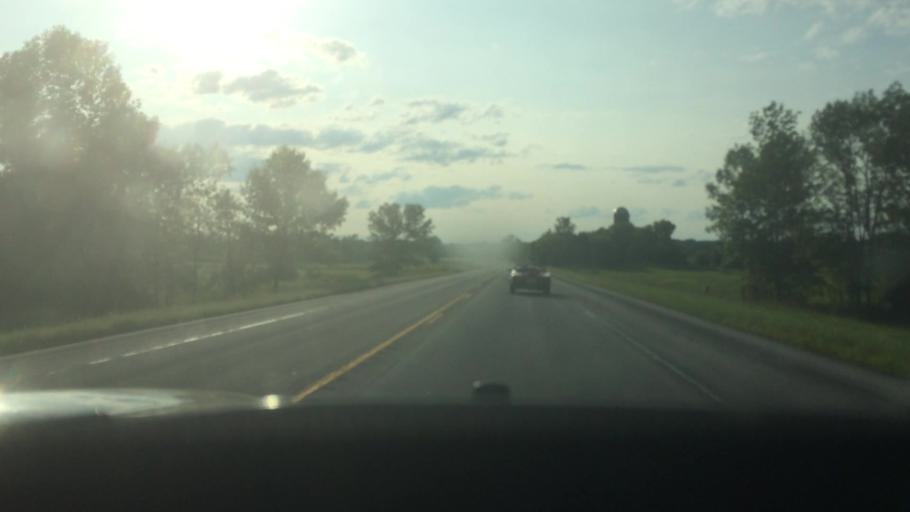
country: US
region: New York
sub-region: St. Lawrence County
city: Canton
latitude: 44.6346
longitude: -75.2572
